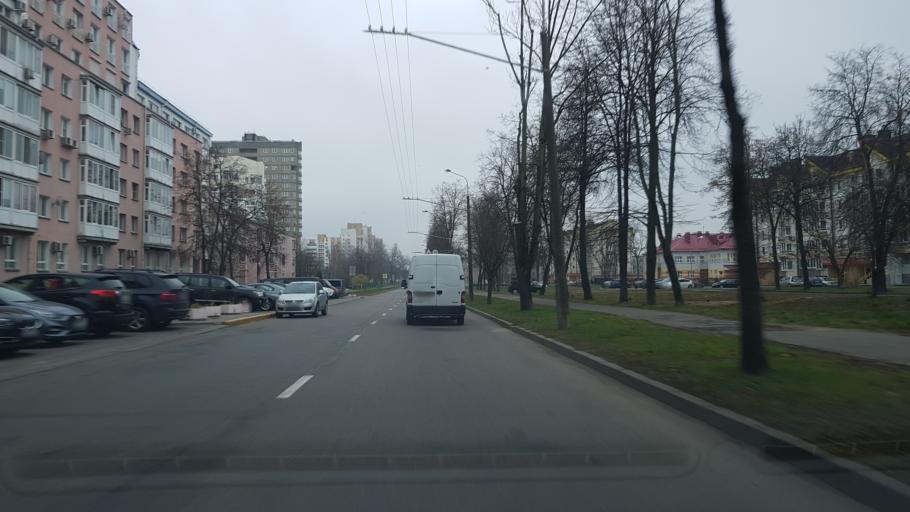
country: BY
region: Minsk
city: Minsk
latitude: 53.9299
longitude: 27.5409
